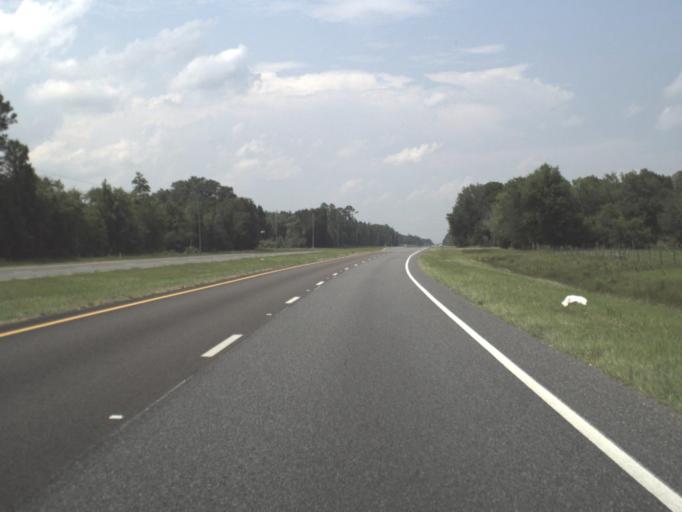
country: US
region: Florida
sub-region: Putnam County
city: Palatka
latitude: 29.8126
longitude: -81.6598
